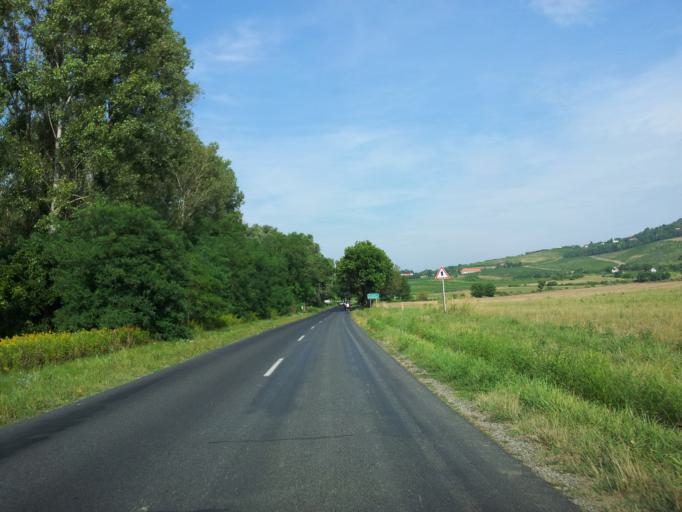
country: HU
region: Veszprem
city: Badacsonytomaj
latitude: 46.8568
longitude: 17.5110
